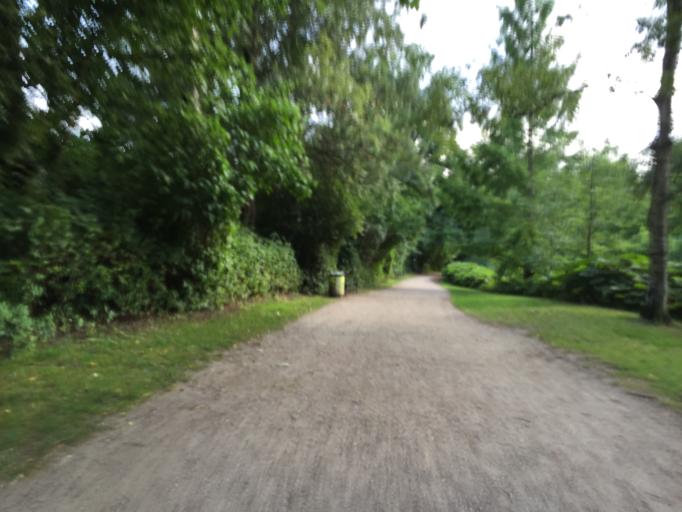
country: DK
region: Capital Region
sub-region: Kobenhavn
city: Christianshavn
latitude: 55.6914
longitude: 12.5846
